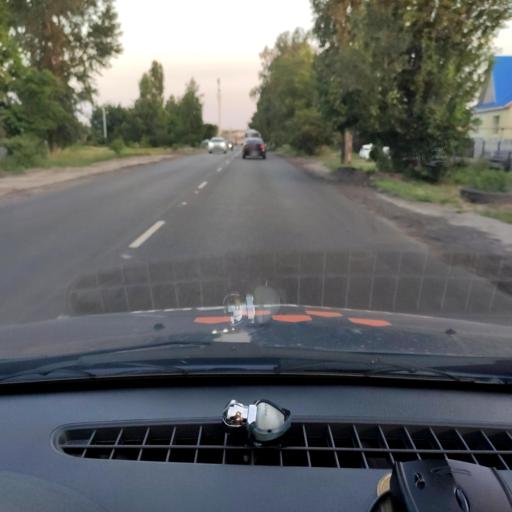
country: RU
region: Voronezj
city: Maslovka
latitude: 51.5420
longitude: 39.2329
